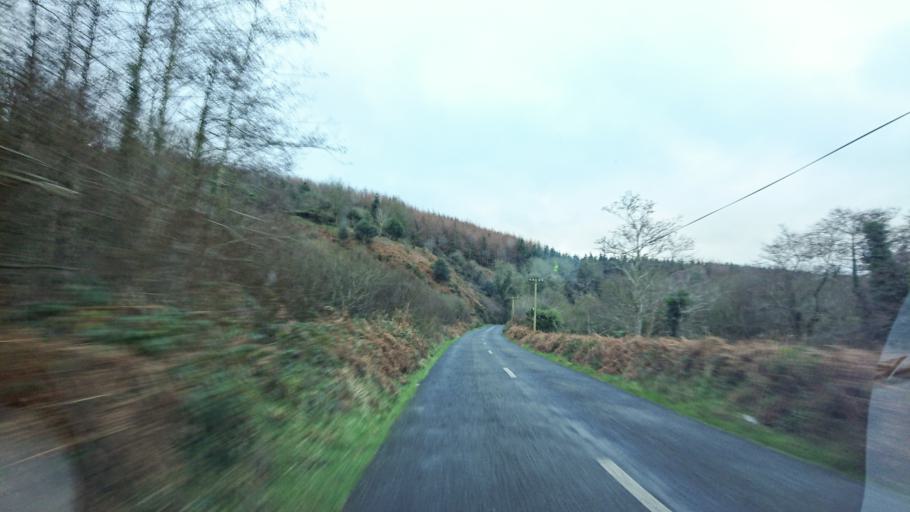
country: IE
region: Munster
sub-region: Waterford
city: Portlaw
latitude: 52.2142
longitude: -7.4192
